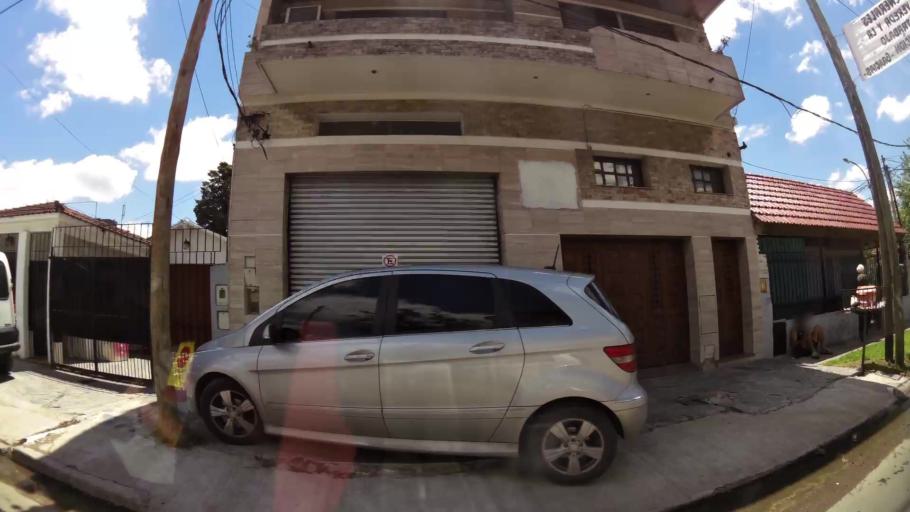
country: AR
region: Buenos Aires
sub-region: Partido de Lomas de Zamora
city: Lomas de Zamora
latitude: -34.7295
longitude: -58.4131
